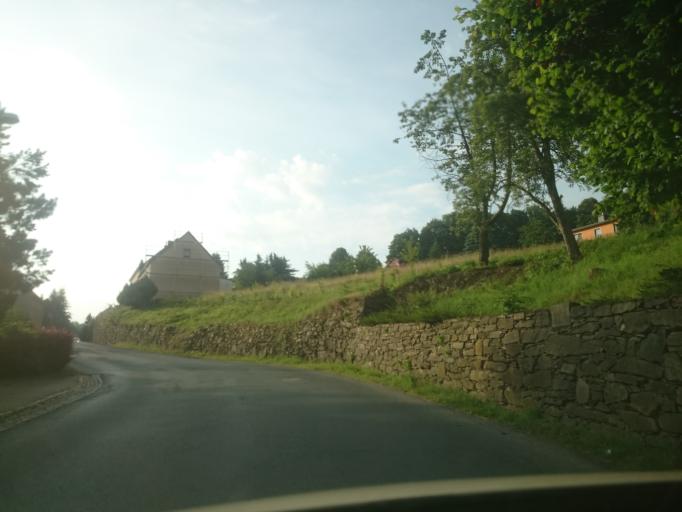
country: DE
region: Saxony
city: Grunhainichen
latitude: 50.7730
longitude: 13.1752
